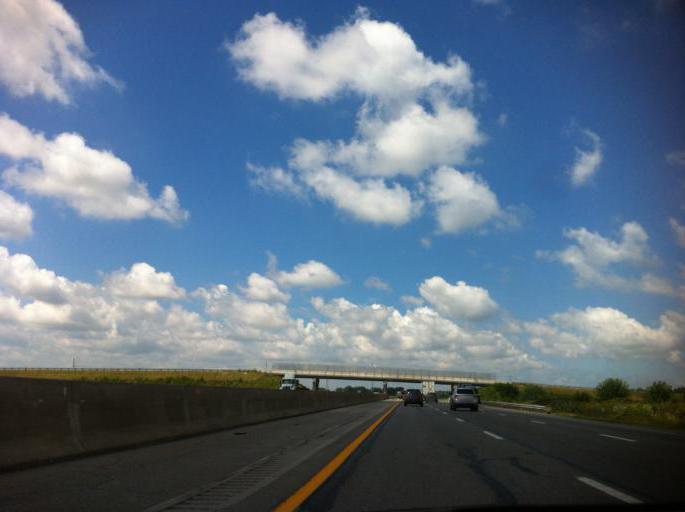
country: US
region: Ohio
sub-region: Erie County
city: Milan
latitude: 41.3335
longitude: -82.6712
